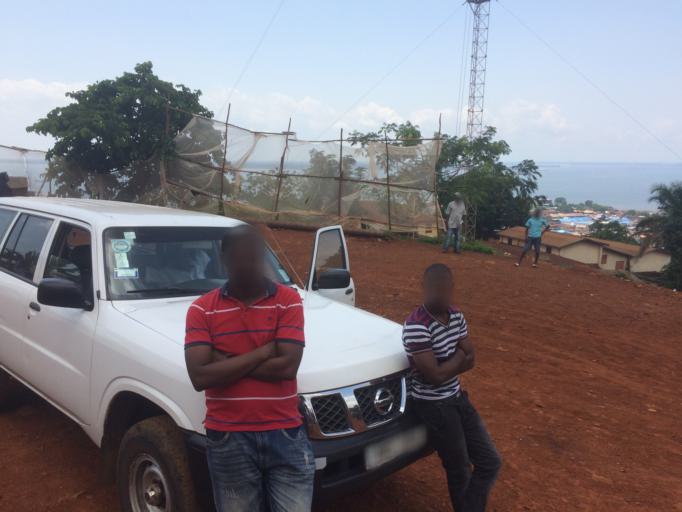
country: SL
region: Western Area
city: Freetown
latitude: 8.4689
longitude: -13.1979
